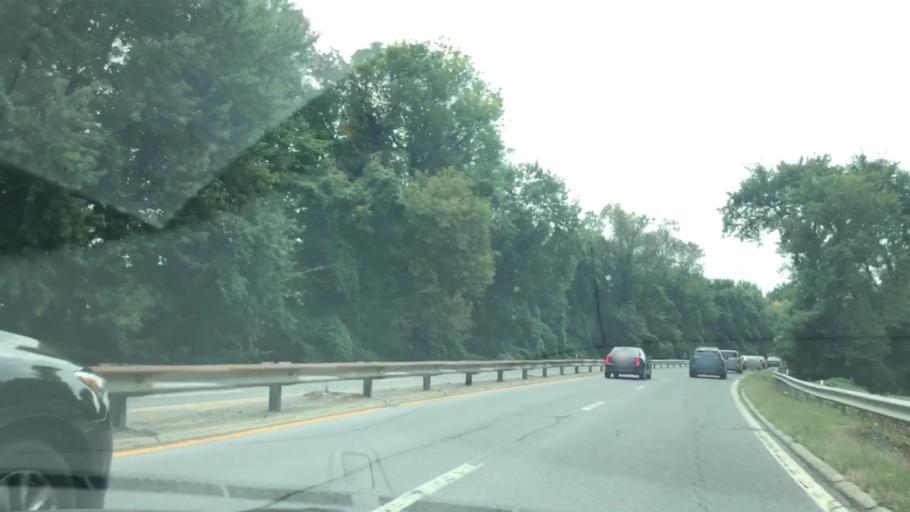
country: US
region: New York
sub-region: Westchester County
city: Hastings-on-Hudson
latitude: 40.9735
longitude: -73.8685
